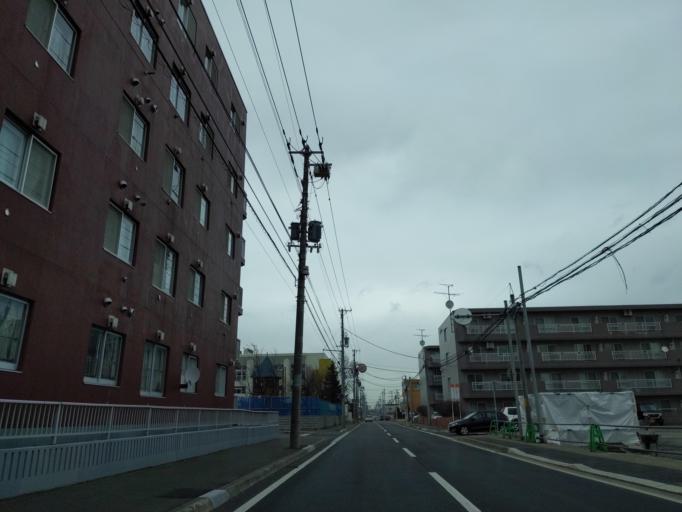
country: JP
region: Hokkaido
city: Sapporo
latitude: 43.0871
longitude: 141.3977
